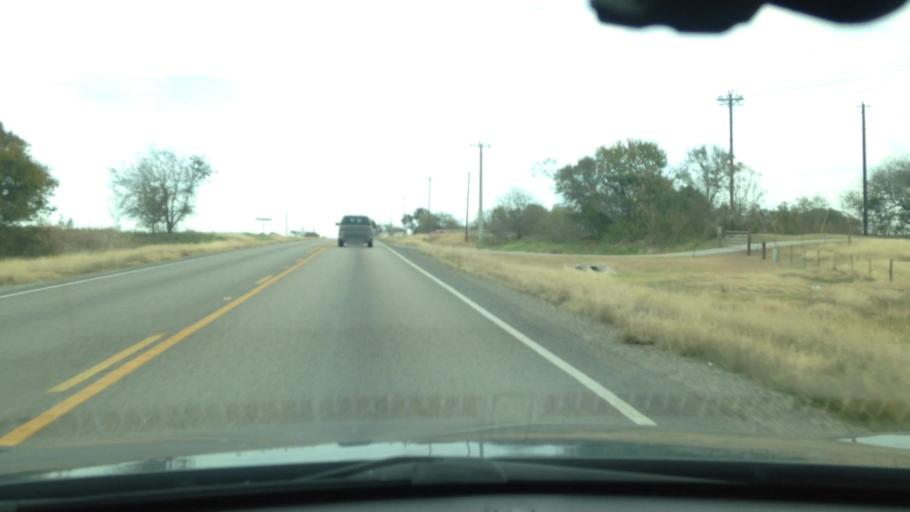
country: US
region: Texas
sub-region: Caldwell County
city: Uhland
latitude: 29.9207
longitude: -97.8397
